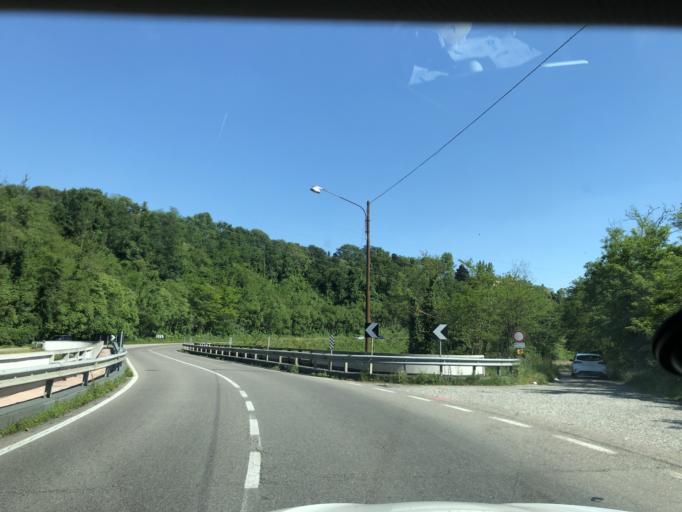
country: IT
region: Lombardy
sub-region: Provincia di Varese
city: Vizzola Ticino
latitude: 45.5868
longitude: 8.7062
